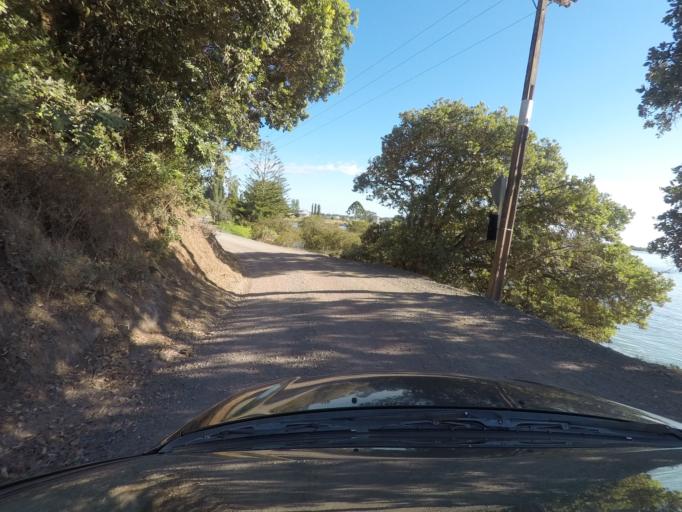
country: NZ
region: Northland
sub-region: Far North District
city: Paihia
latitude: -35.2541
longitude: 174.0722
